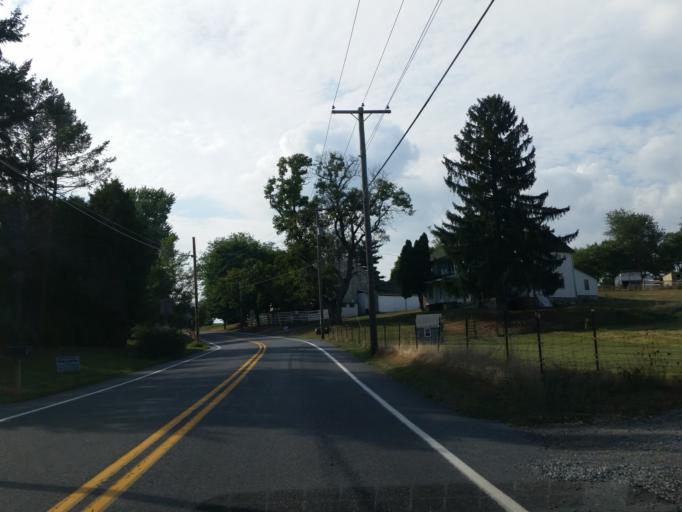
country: US
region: Pennsylvania
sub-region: Lancaster County
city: Manheim
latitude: 40.1870
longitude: -76.4708
